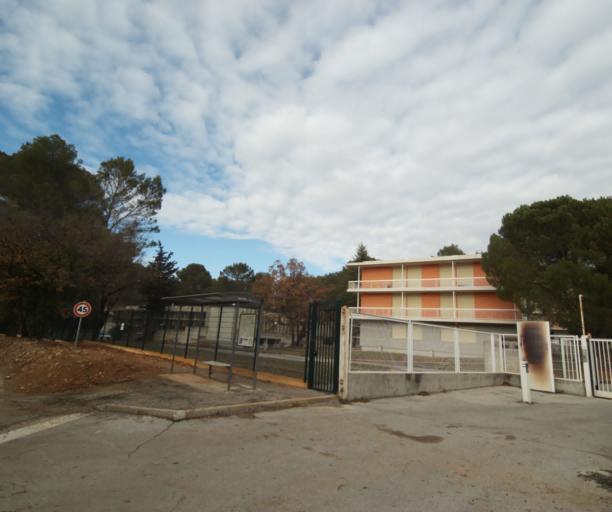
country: FR
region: Provence-Alpes-Cote d'Azur
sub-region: Departement du Var
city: Trans-en-Provence
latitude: 43.5230
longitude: 6.4994
